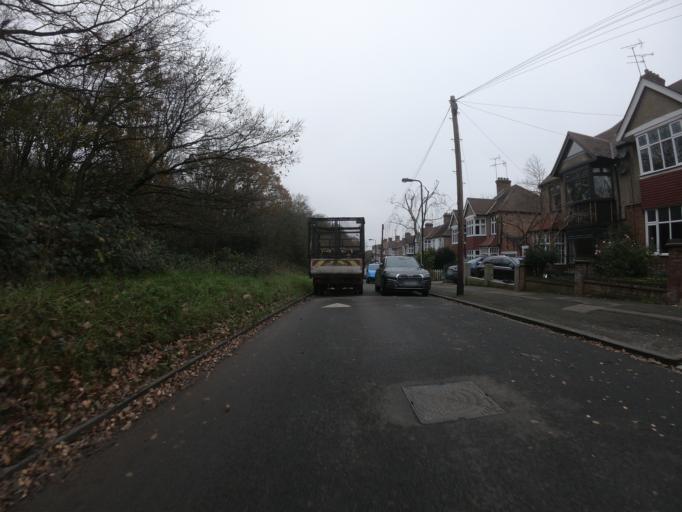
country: GB
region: England
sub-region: Greater London
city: Woodford Green
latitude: 51.6027
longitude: 0.0072
